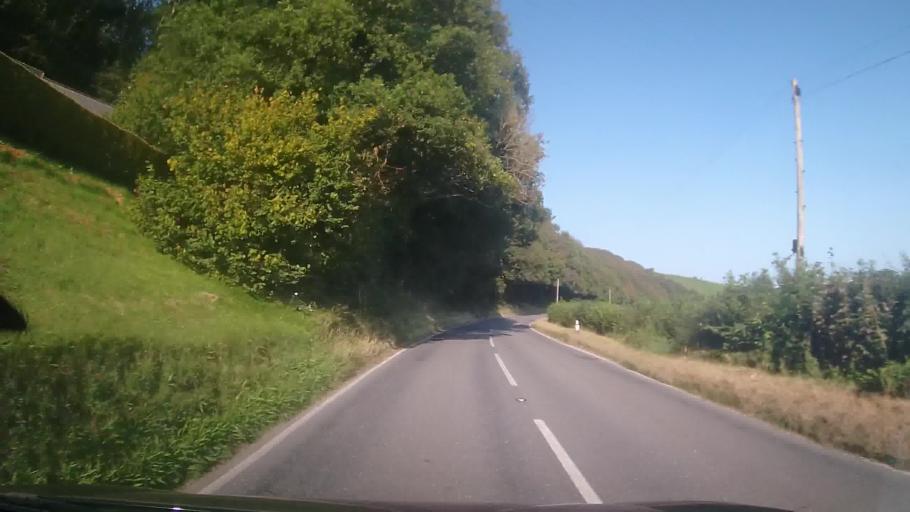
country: GB
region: Wales
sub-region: County of Ceredigion
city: Llangybi
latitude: 52.1412
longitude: -4.0705
